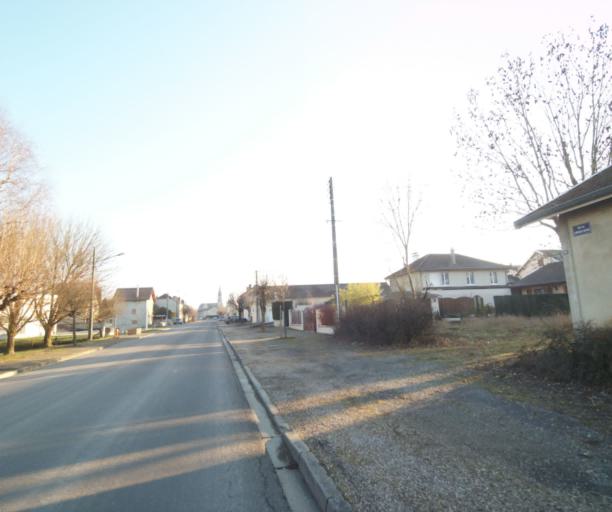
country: FR
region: Champagne-Ardenne
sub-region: Departement de la Haute-Marne
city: Bienville
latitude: 48.5893
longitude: 5.0341
